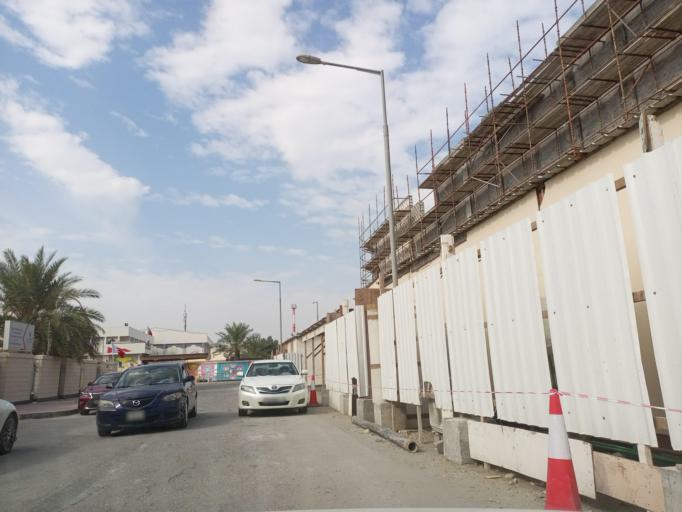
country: BH
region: Muharraq
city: Al Hadd
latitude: 26.2541
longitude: 50.6438
